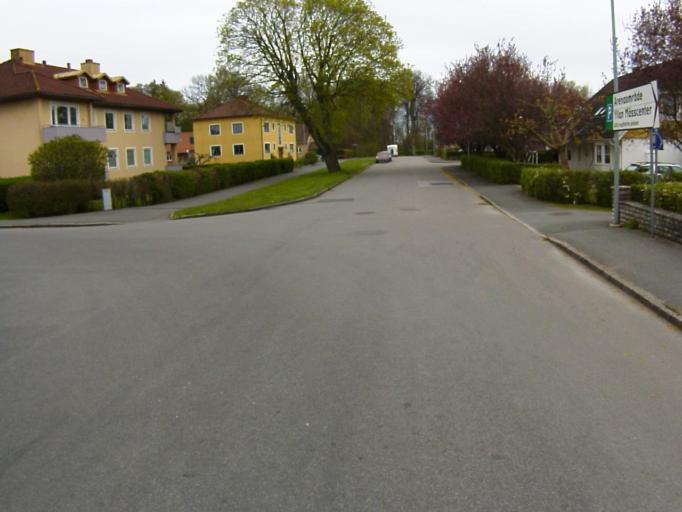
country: SE
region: Skane
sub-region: Kristianstads Kommun
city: Kristianstad
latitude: 56.0203
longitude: 14.1620
